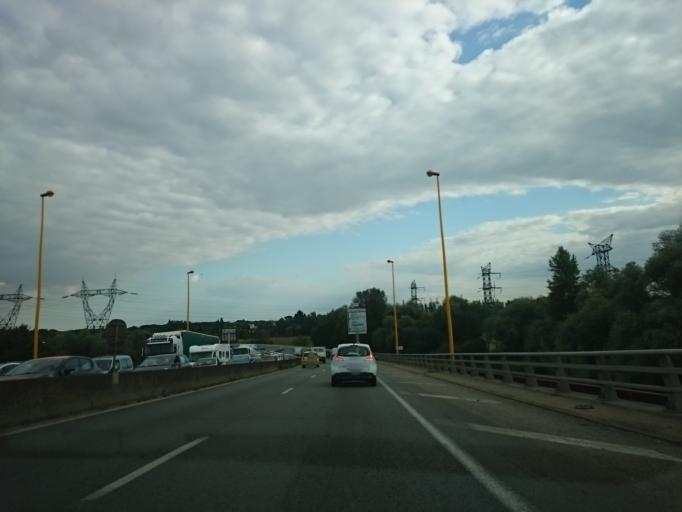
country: FR
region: Pays de la Loire
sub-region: Departement de la Loire-Atlantique
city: Bouguenais
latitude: 47.1848
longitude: -1.6137
